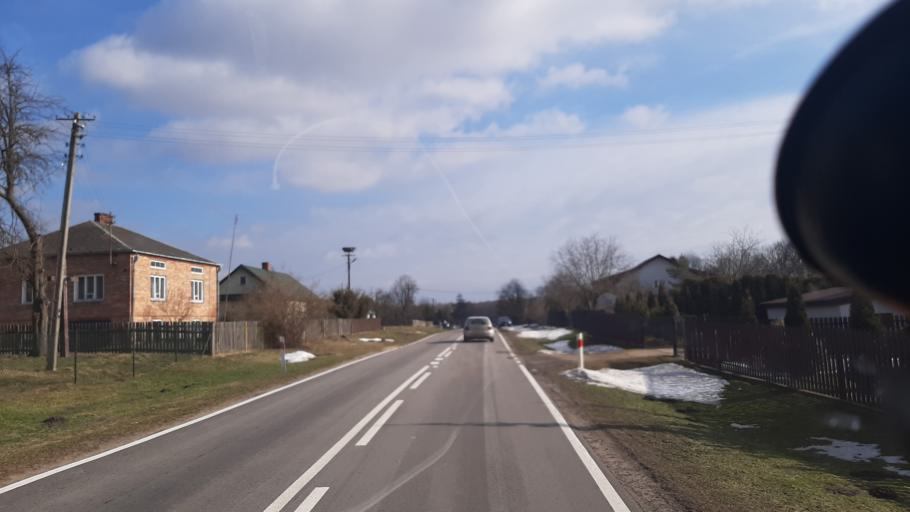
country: PL
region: Lublin Voivodeship
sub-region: Powiat parczewski
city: Sosnowica
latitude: 51.4973
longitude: 23.1688
